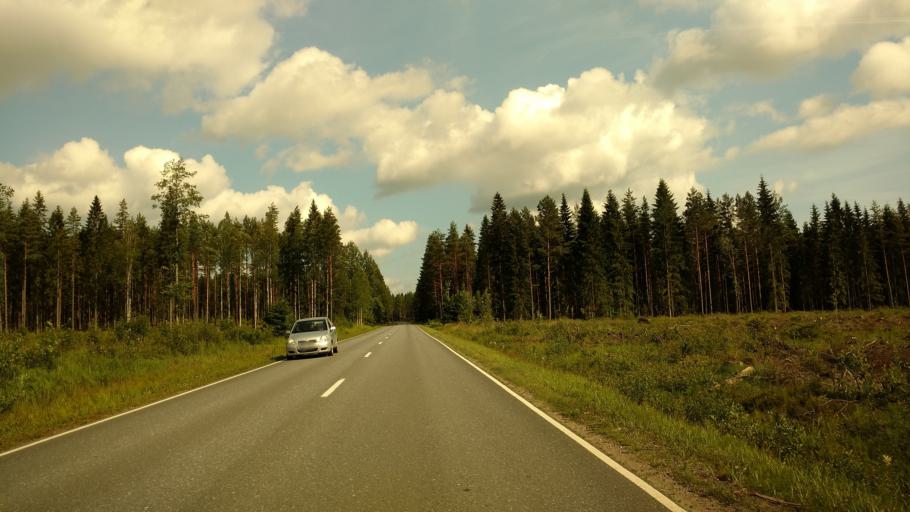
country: FI
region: Varsinais-Suomi
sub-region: Loimaa
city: Koski Tl
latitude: 60.6084
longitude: 23.1216
